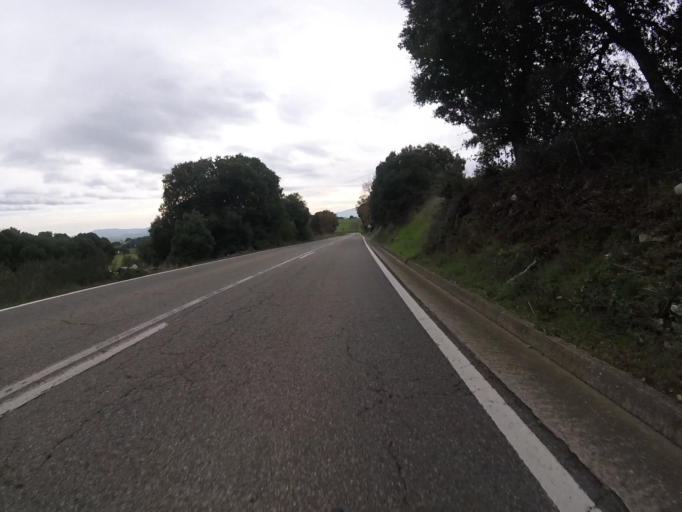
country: ES
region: Navarre
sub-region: Provincia de Navarra
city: Lezaun
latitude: 42.7427
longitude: -2.0207
